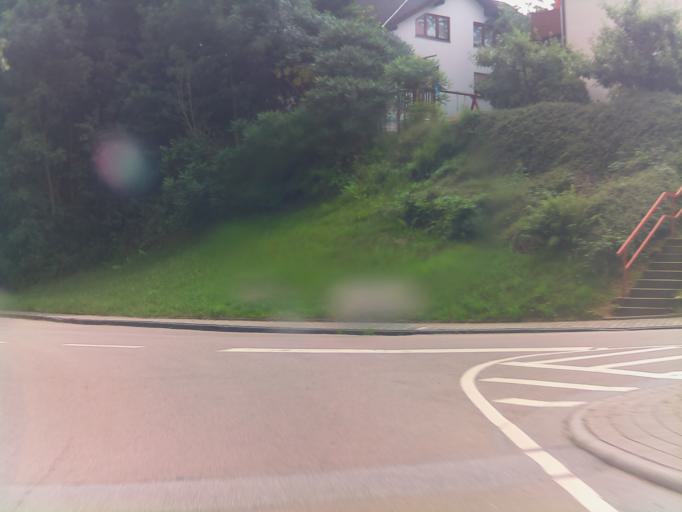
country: DE
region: Hesse
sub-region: Regierungsbezirk Darmstadt
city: Rimbach
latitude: 49.6398
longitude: 8.7564
